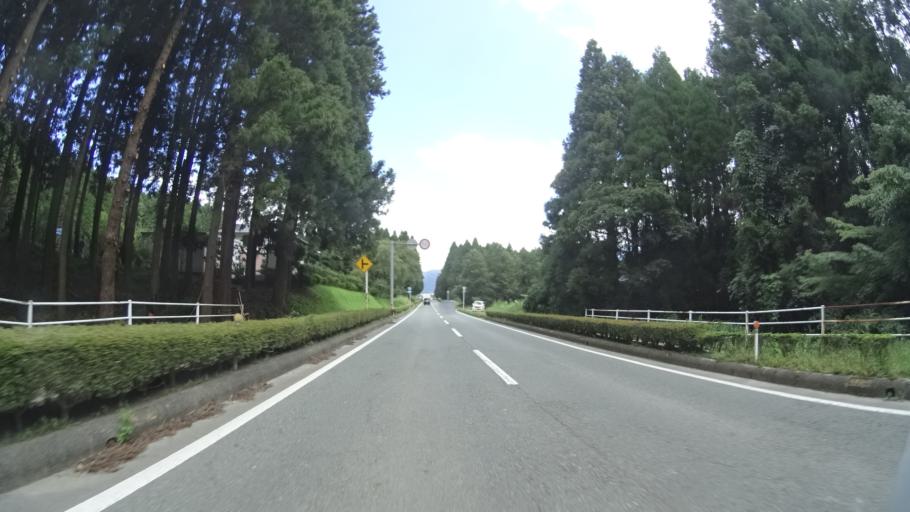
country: JP
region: Kumamoto
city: Aso
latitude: 32.8309
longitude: 131.0846
